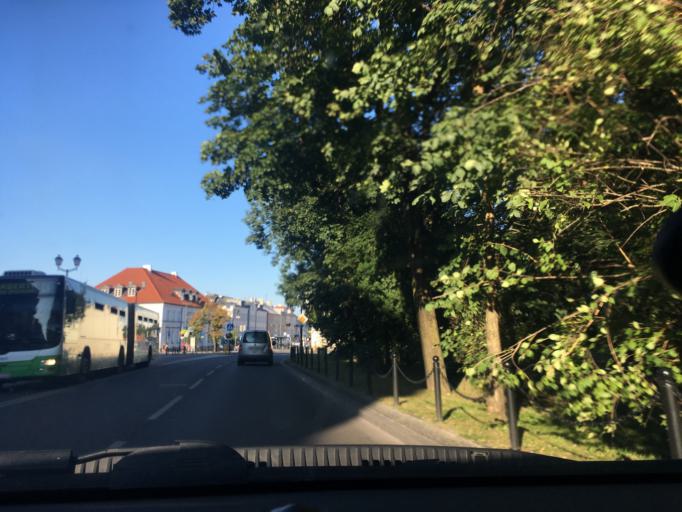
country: PL
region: Podlasie
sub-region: Bialystok
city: Bialystok
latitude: 53.1315
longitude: 23.1625
